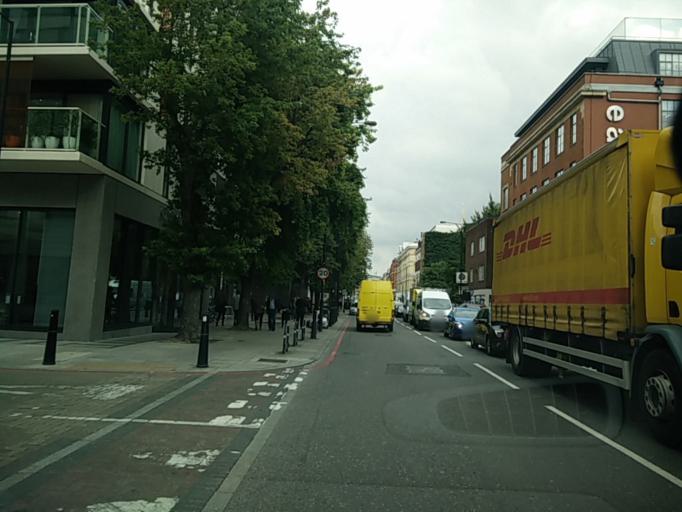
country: GB
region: England
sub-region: Greater London
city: Bethnal Green
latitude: 51.5159
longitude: -0.0723
